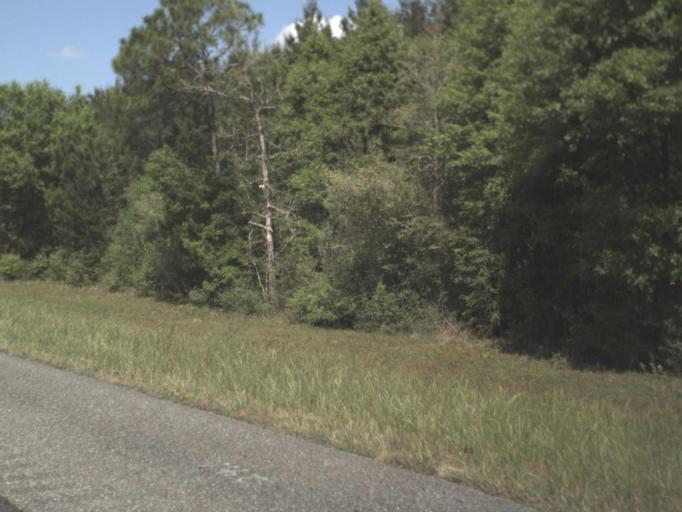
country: US
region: Florida
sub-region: Santa Rosa County
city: East Milton
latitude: 30.6774
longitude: -86.8220
